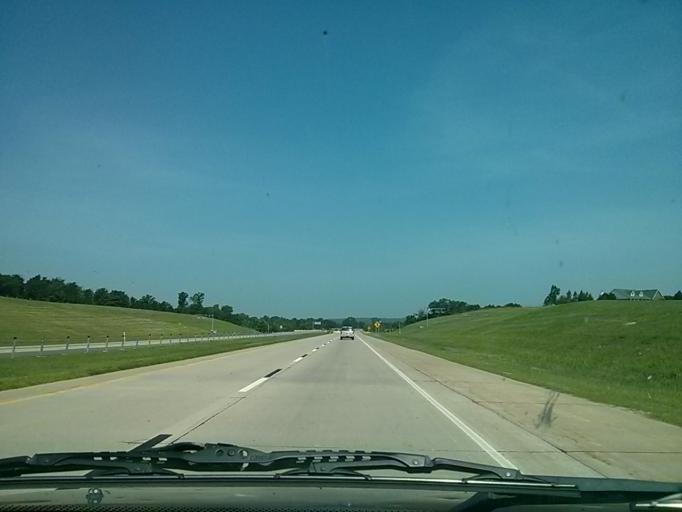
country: US
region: Oklahoma
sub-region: Creek County
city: Sapulpa
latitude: 36.0186
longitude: -96.0663
